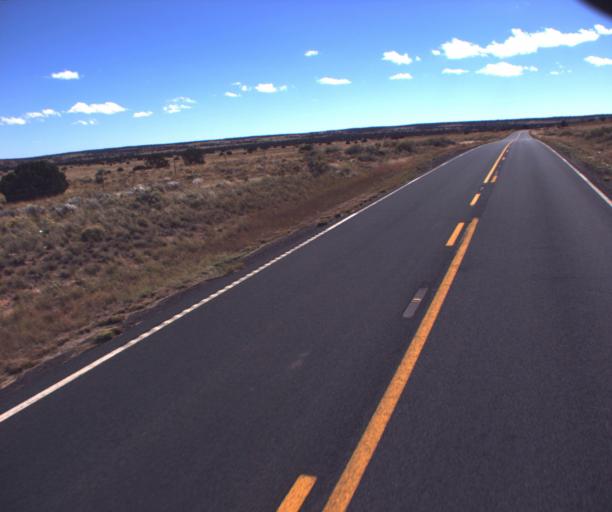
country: US
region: Arizona
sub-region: Apache County
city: Houck
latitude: 35.0109
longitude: -109.2333
